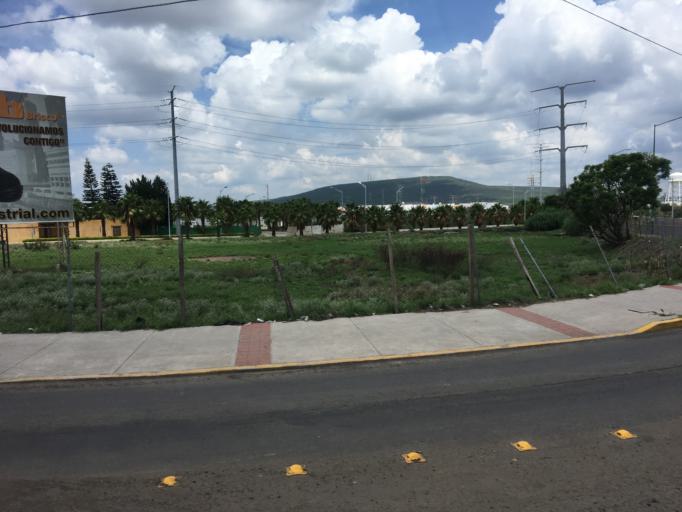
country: MX
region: Guanajuato
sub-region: Irapuato
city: Ex-Hacienda del Copal
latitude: 20.7198
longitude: -101.3478
